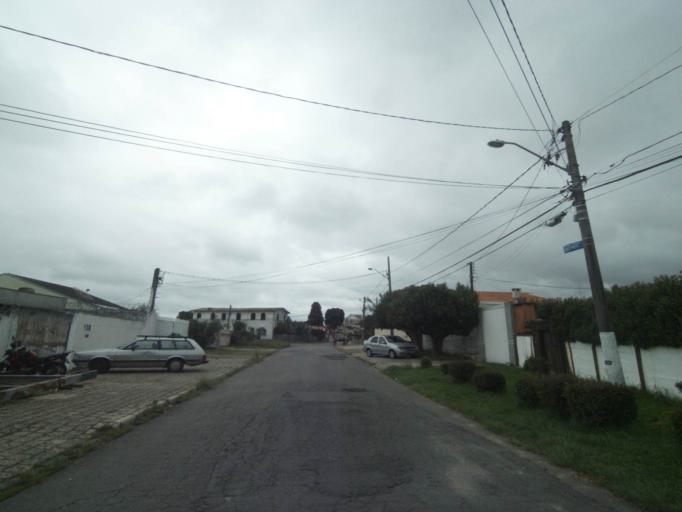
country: BR
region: Parana
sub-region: Curitiba
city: Curitiba
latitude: -25.4902
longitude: -49.2846
